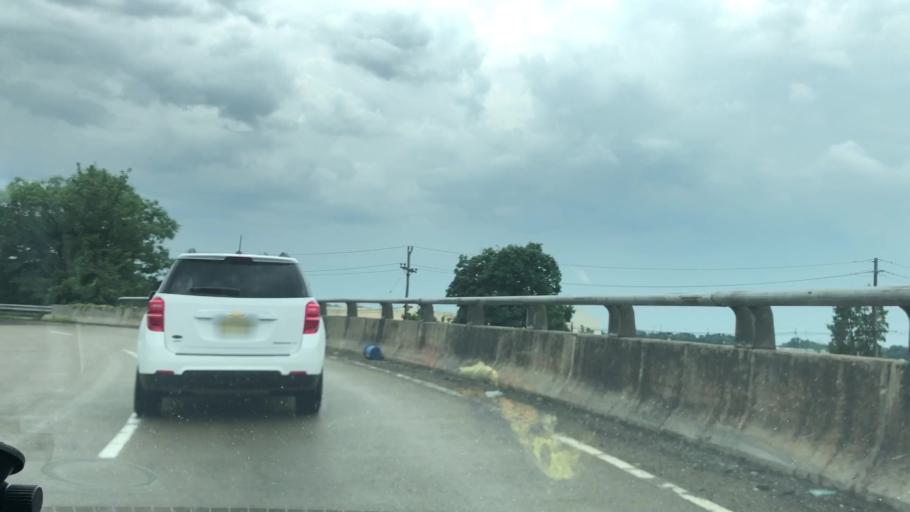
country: US
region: New Jersey
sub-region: Passaic County
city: Singac
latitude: 40.8933
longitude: -74.2557
